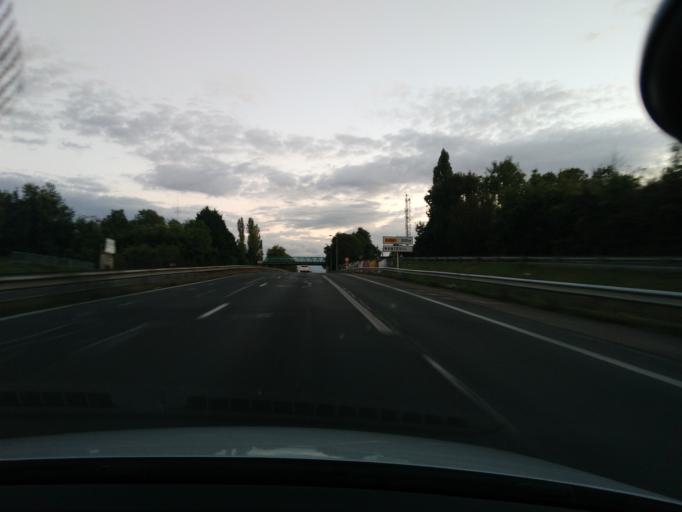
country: FR
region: Ile-de-France
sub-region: Departement de Seine-et-Marne
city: Nanteuil-les-Meaux
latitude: 48.9305
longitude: 2.8802
